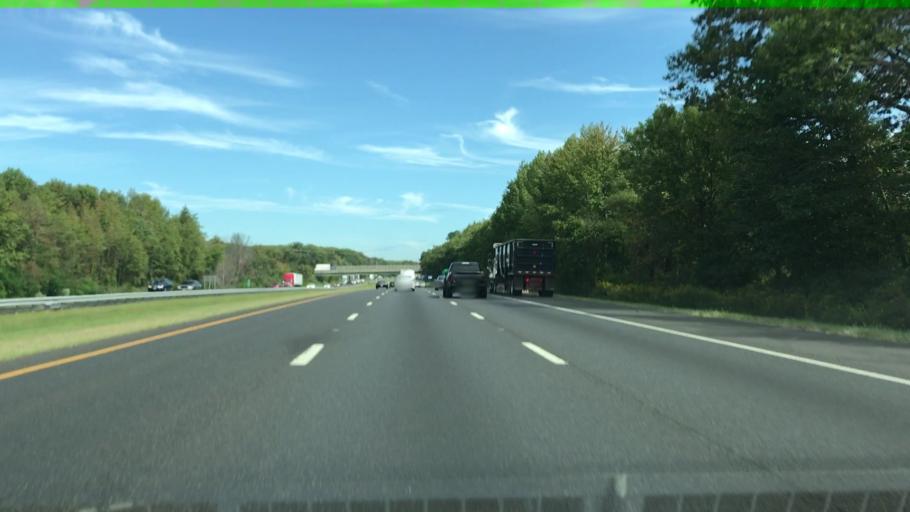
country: US
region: New Jersey
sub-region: Burlington County
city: Willingboro
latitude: 40.0332
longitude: -74.8401
